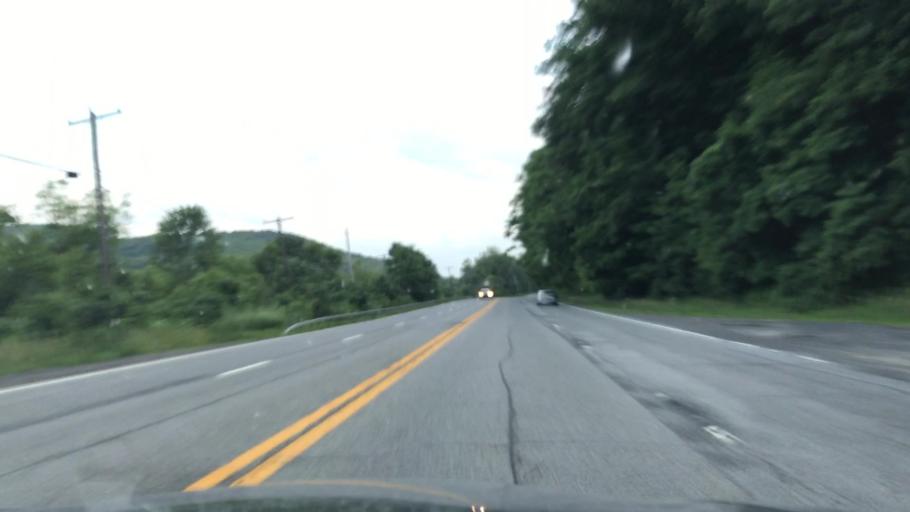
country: US
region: New York
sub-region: Orange County
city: Harriman
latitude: 41.2829
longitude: -74.1473
